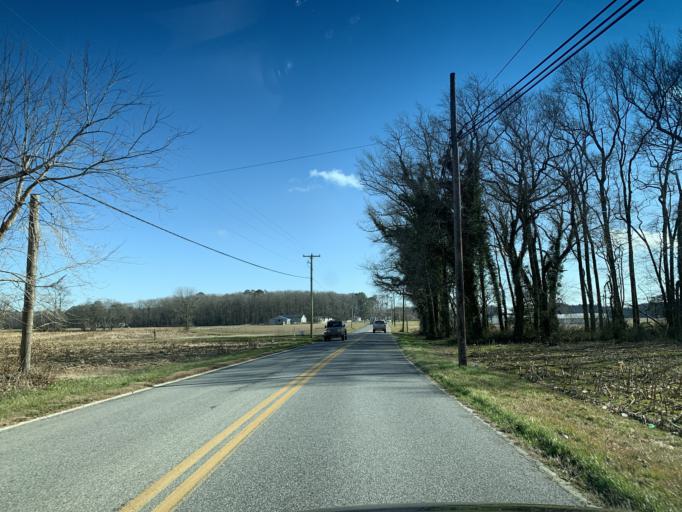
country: US
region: Maryland
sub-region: Worcester County
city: Ocean Pines
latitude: 38.4334
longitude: -75.1805
